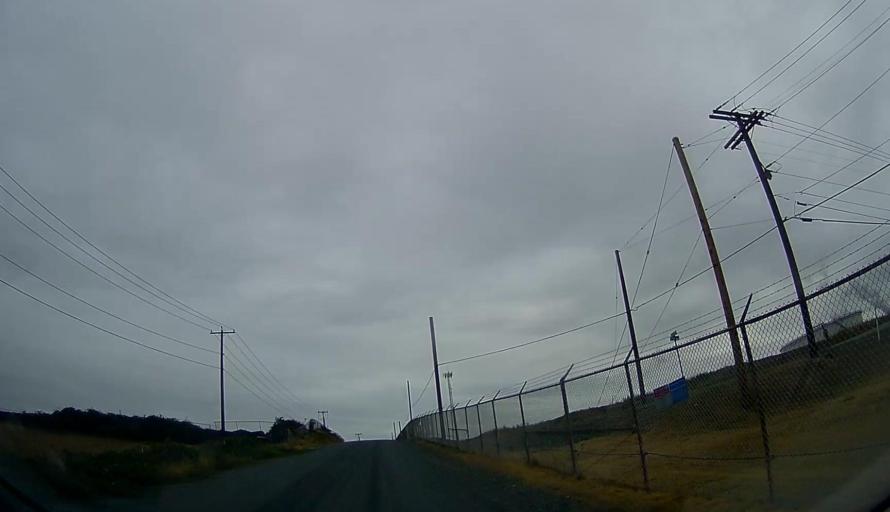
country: US
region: Washington
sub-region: Skagit County
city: Anacortes
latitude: 48.4785
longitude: -122.5667
